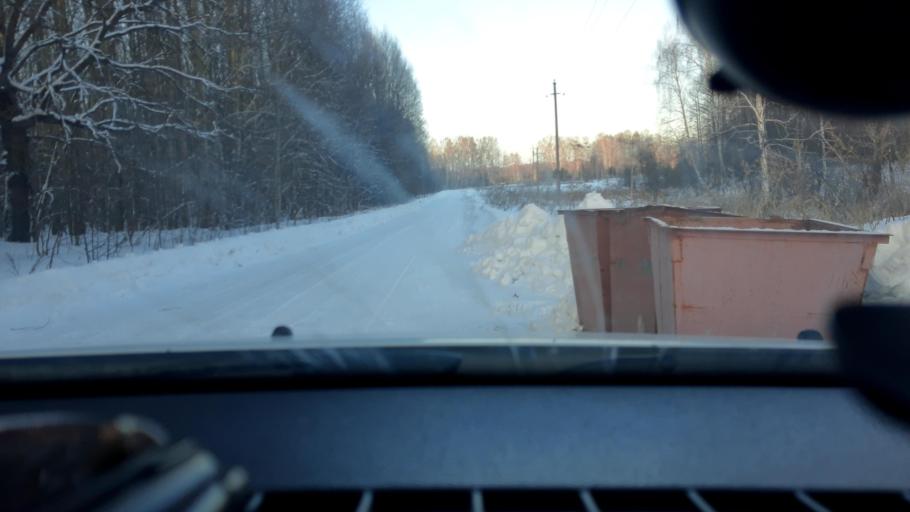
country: RU
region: Bashkortostan
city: Kudeyevskiy
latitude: 54.8002
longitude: 56.6760
